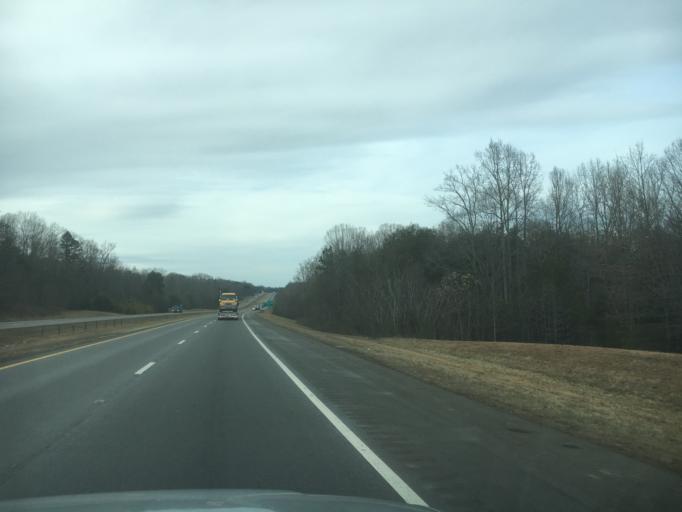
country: US
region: North Carolina
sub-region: Catawba County
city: Mountain View
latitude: 35.6633
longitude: -81.3251
